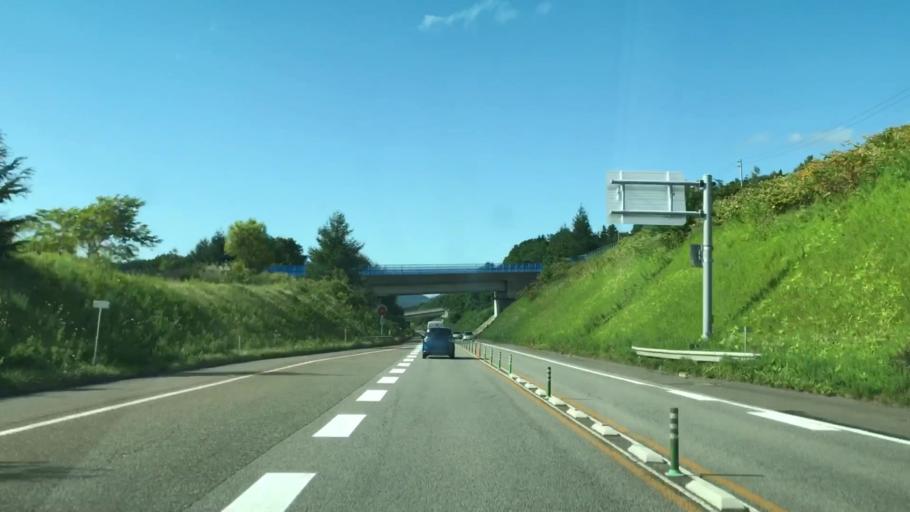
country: JP
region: Hokkaido
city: Date
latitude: 42.4693
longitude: 140.9069
